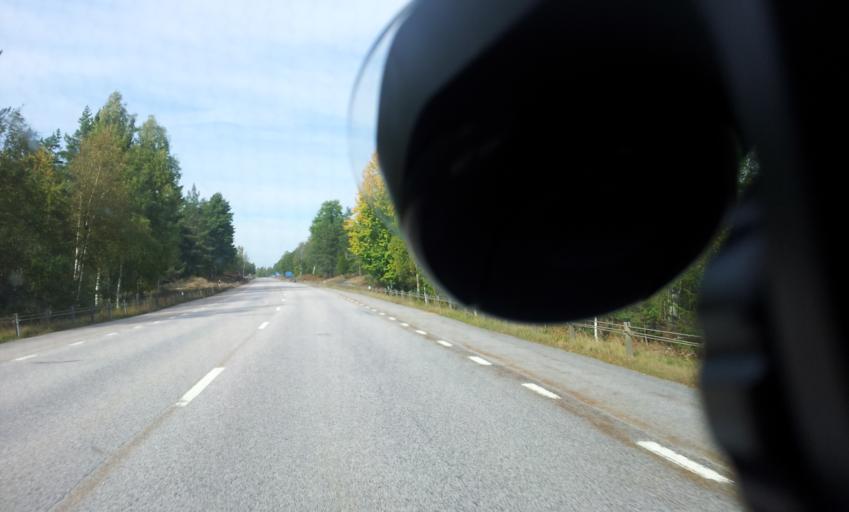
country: SE
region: Kalmar
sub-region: Vasterviks Kommun
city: Ankarsrum
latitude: 57.5181
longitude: 16.4978
